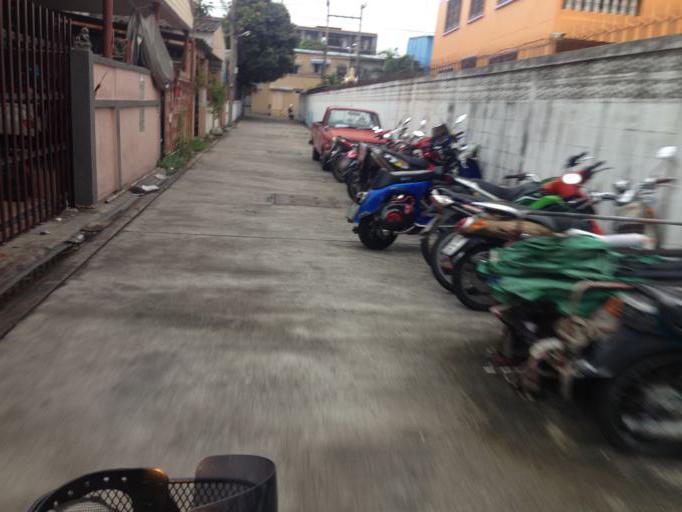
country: TH
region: Chon Buri
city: Chon Buri
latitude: 13.2878
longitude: 100.9285
